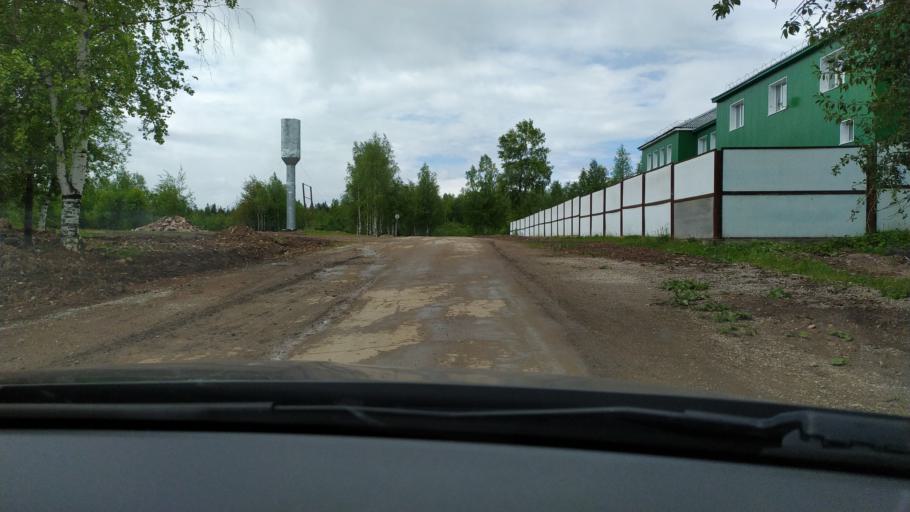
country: RU
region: Perm
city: Gremyachinsk
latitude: 58.5106
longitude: 57.8277
